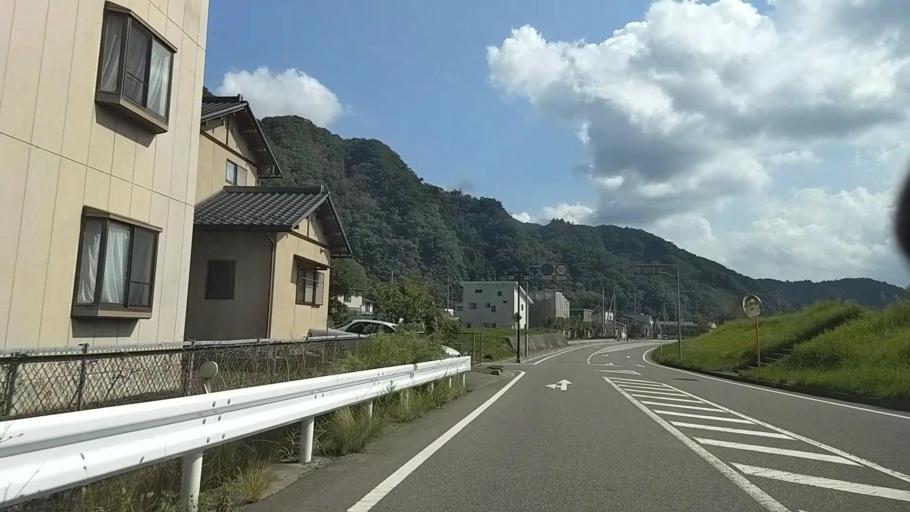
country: JP
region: Shizuoka
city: Fujinomiya
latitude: 35.3705
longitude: 138.4538
